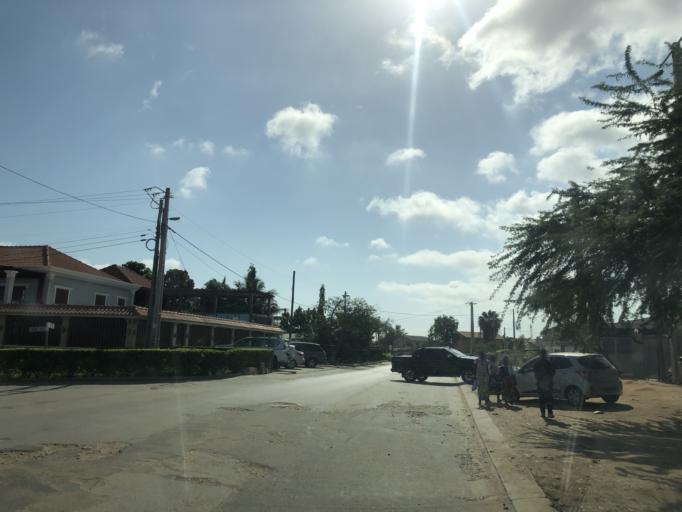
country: AO
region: Luanda
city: Luanda
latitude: -8.9074
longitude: 13.2312
